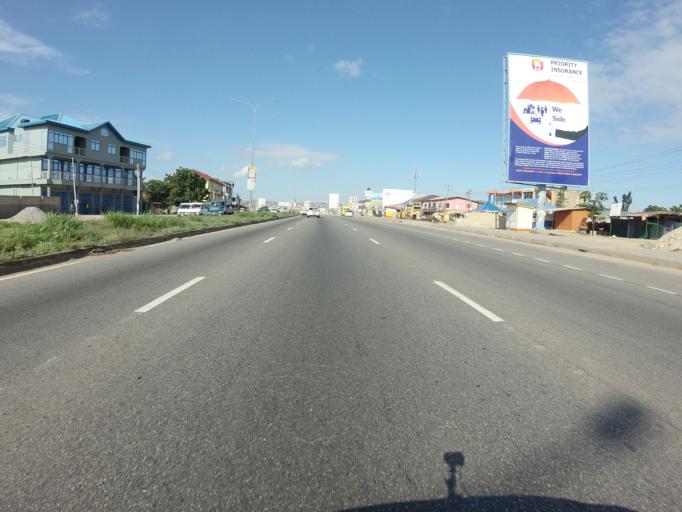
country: GH
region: Greater Accra
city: Gbawe
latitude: 5.5530
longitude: -0.3240
